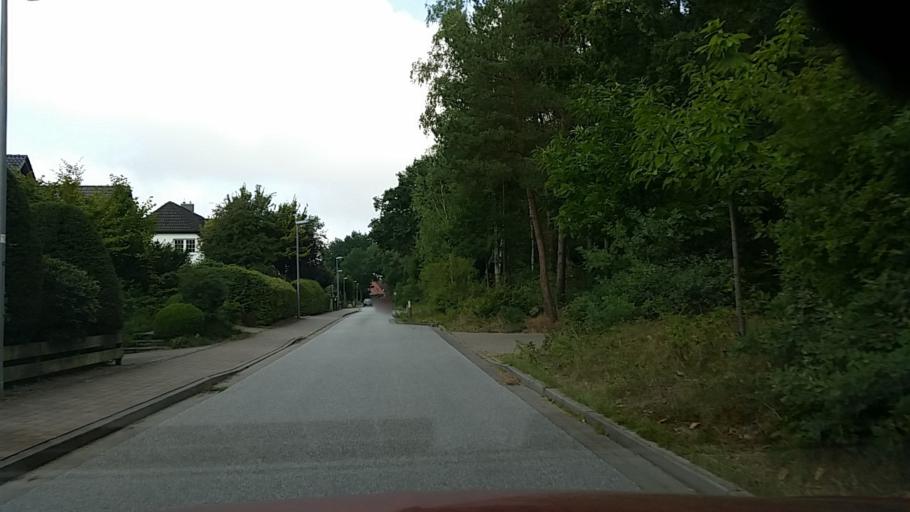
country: DE
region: Schleswig-Holstein
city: Wedel
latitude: 53.5997
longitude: 9.7264
